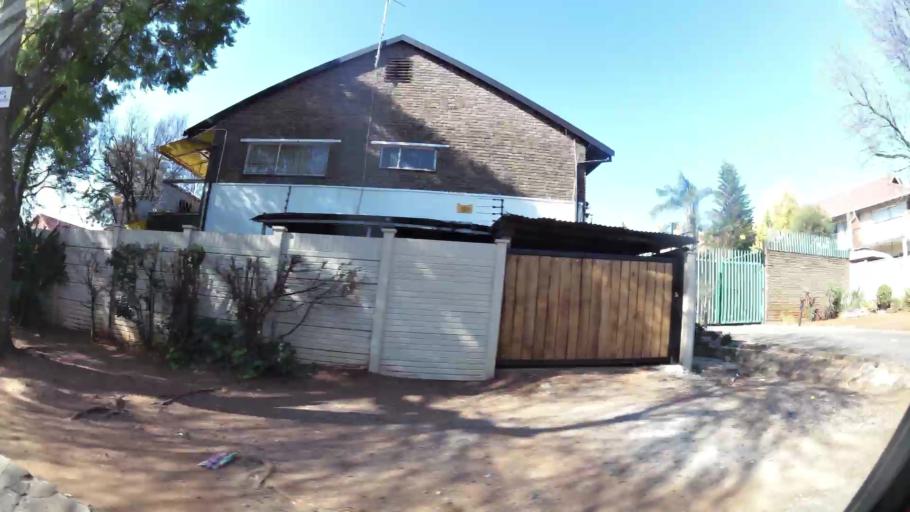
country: ZA
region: Gauteng
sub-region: City of Johannesburg Metropolitan Municipality
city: Roodepoort
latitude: -26.1246
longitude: 27.9688
